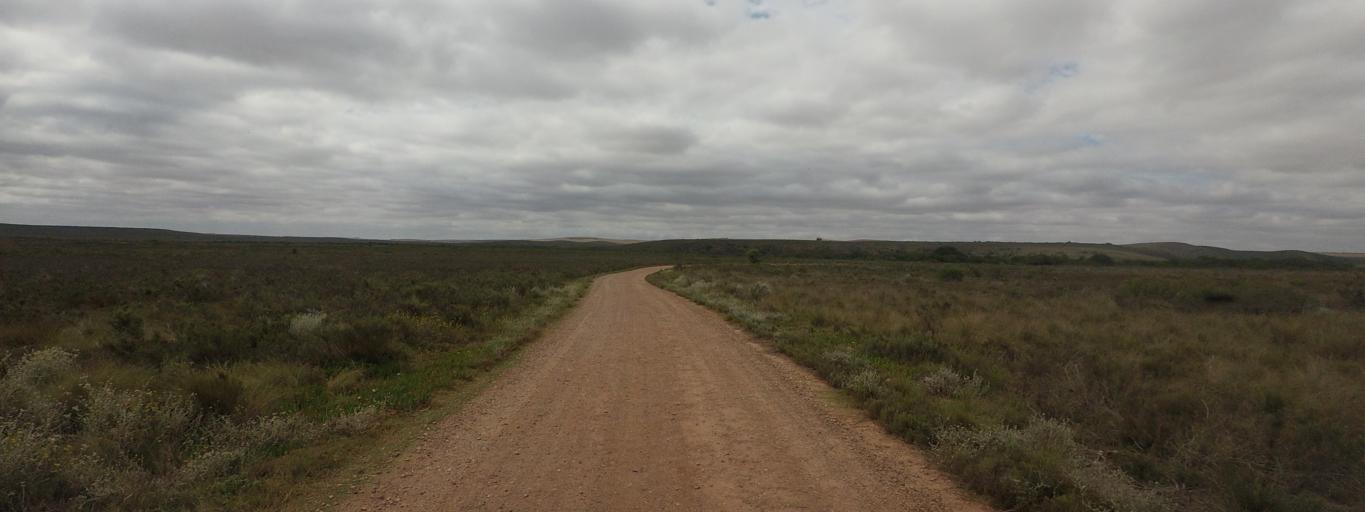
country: ZA
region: Western Cape
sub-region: Overberg District Municipality
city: Swellendam
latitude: -34.0630
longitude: 20.4388
